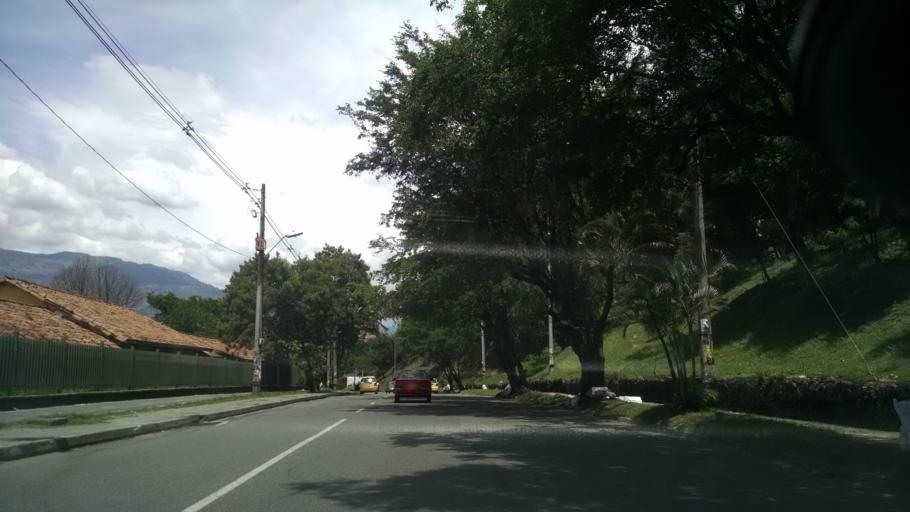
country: CO
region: Antioquia
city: Medellin
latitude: 6.2362
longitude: -75.5827
